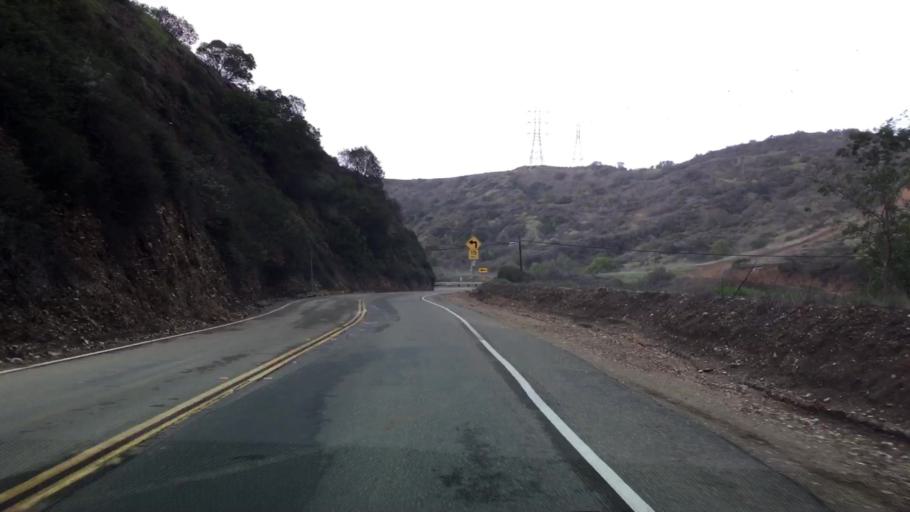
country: US
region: California
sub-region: Los Angeles County
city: Whittier
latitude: 33.9937
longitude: -118.0074
